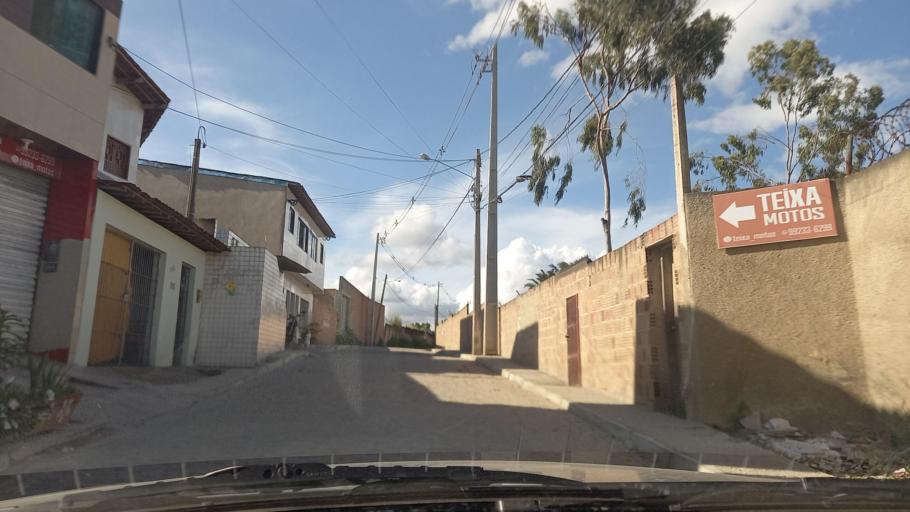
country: BR
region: Pernambuco
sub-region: Gravata
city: Gravata
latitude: -8.1982
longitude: -35.5664
